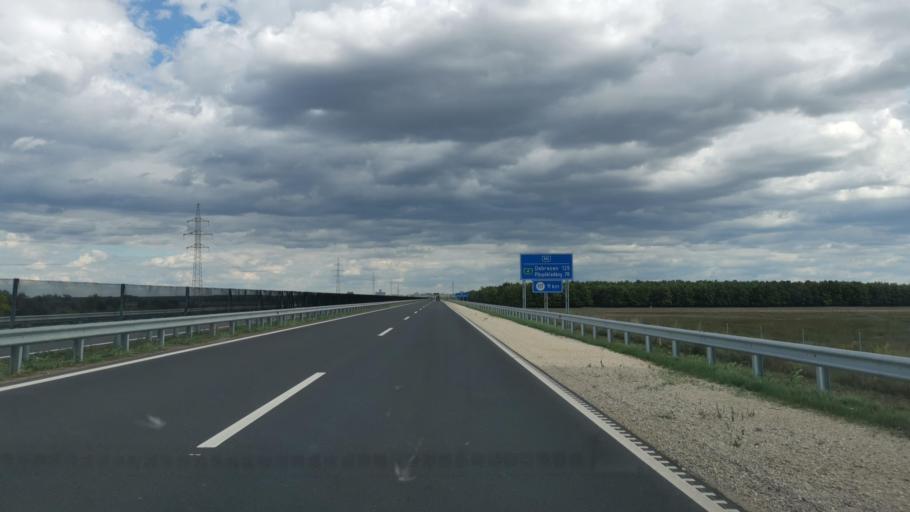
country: HU
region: Jasz-Nagykun-Szolnok
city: Szolnok
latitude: 47.2225
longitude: 20.2272
